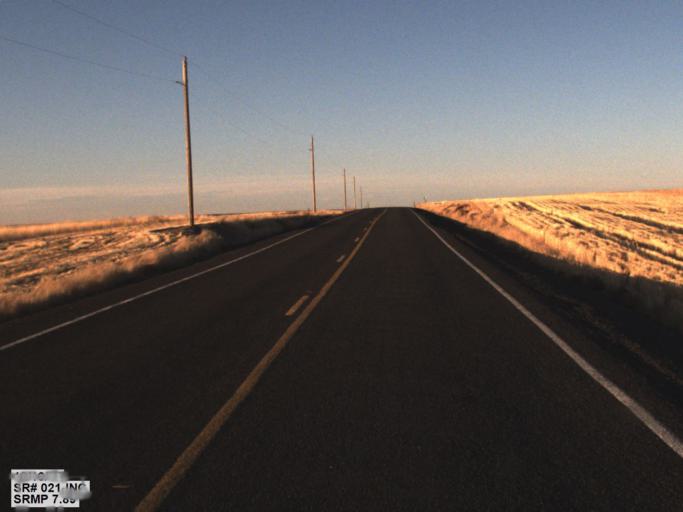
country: US
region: Washington
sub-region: Franklin County
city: Connell
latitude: 46.7405
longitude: -118.5477
